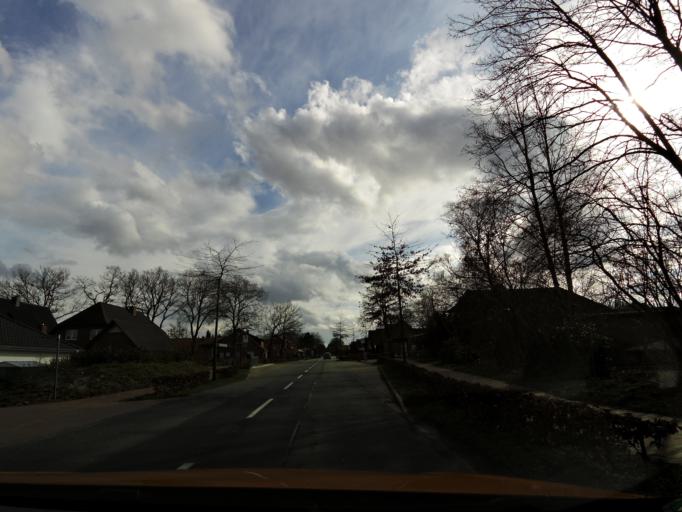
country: DE
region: Lower Saxony
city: Dotlingen
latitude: 52.9777
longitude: 8.3975
